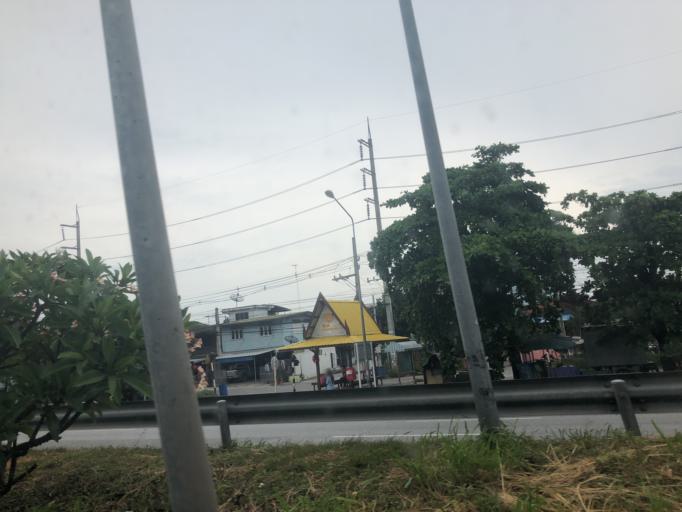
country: TH
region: Chon Buri
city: Bang Lamung
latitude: 13.0684
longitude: 100.9243
